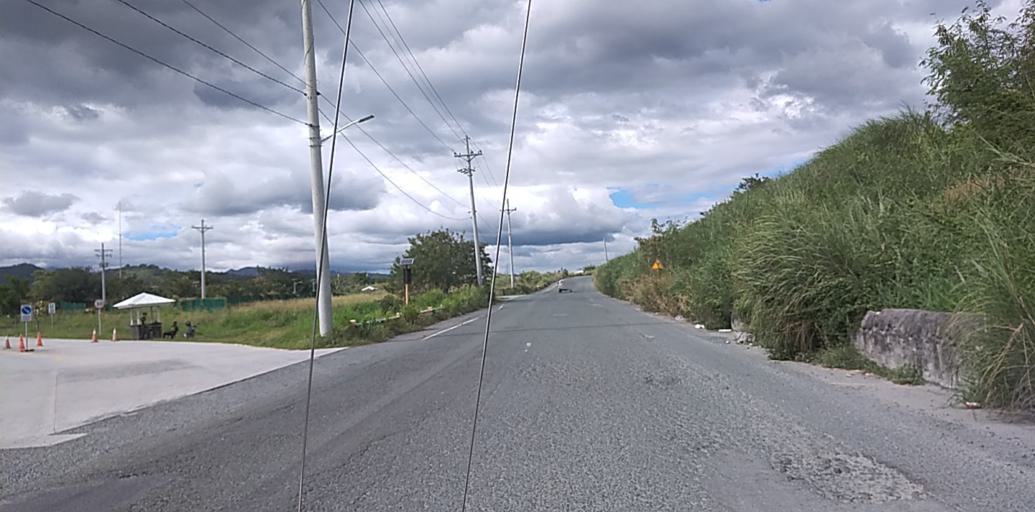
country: PH
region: Central Luzon
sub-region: Province of Pampanga
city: Dolores
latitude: 15.1156
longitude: 120.5146
